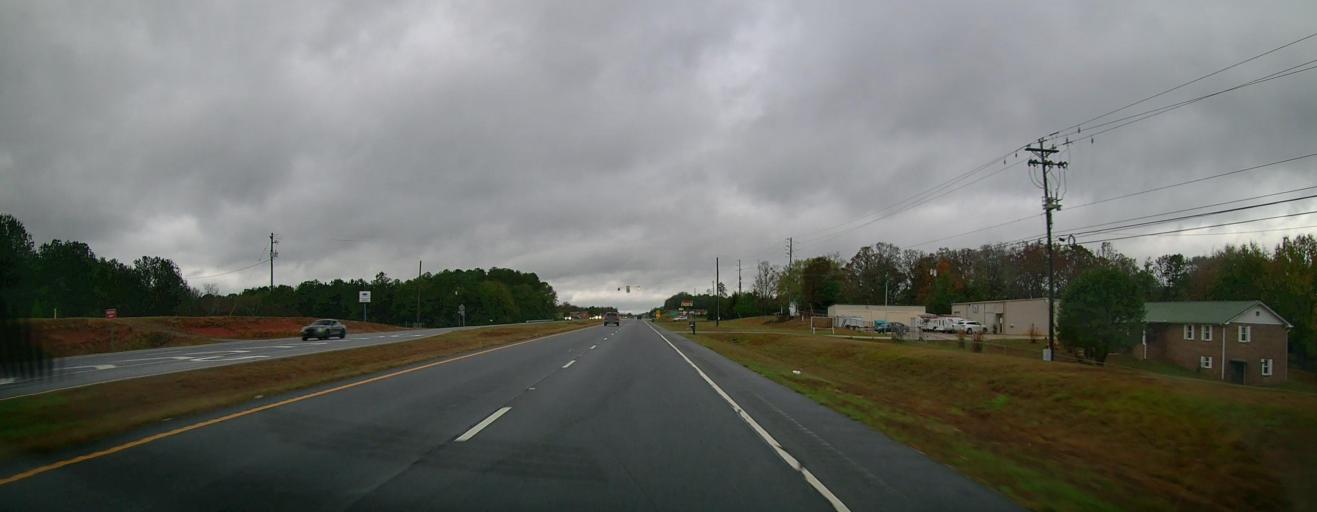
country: US
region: Georgia
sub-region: Jackson County
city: Nicholson
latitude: 34.1450
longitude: -83.4364
